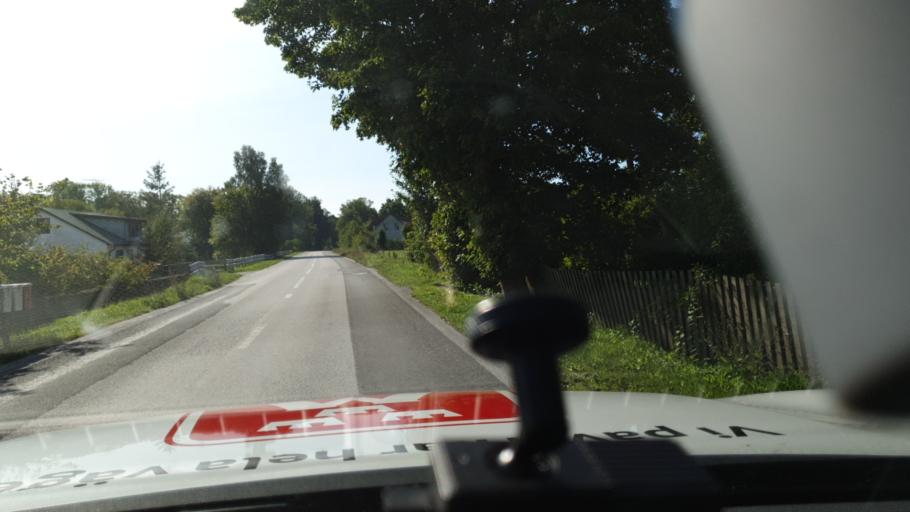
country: SE
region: Gotland
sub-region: Gotland
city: Hemse
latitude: 57.0966
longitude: 18.3037
